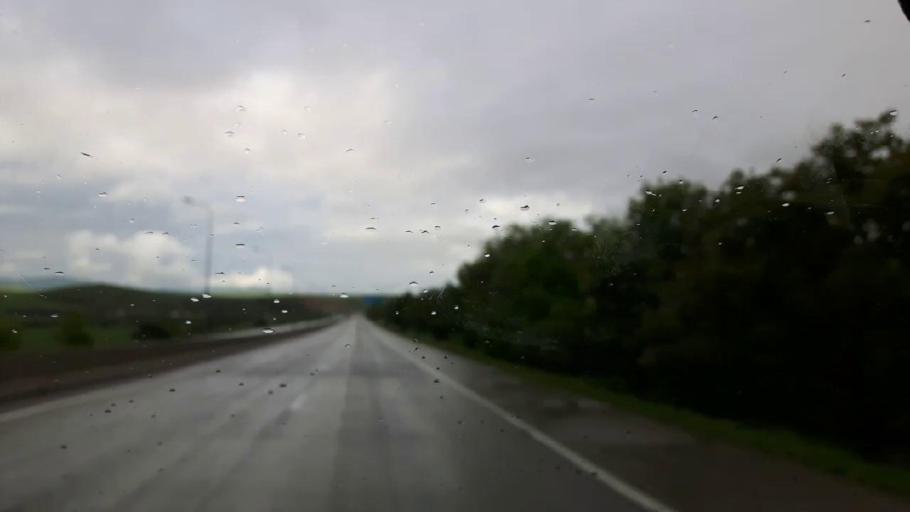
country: GE
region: Shida Kartli
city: Kaspi
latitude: 42.0026
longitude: 44.3748
